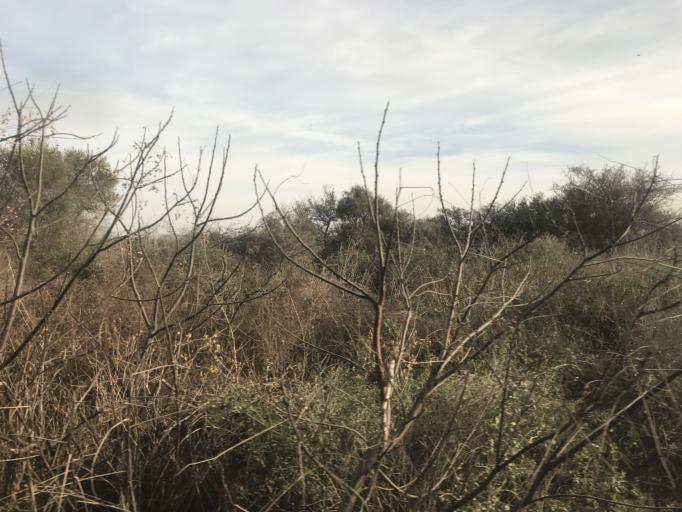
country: AR
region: Cordoba
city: Pilar
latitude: -31.6915
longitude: -63.8775
